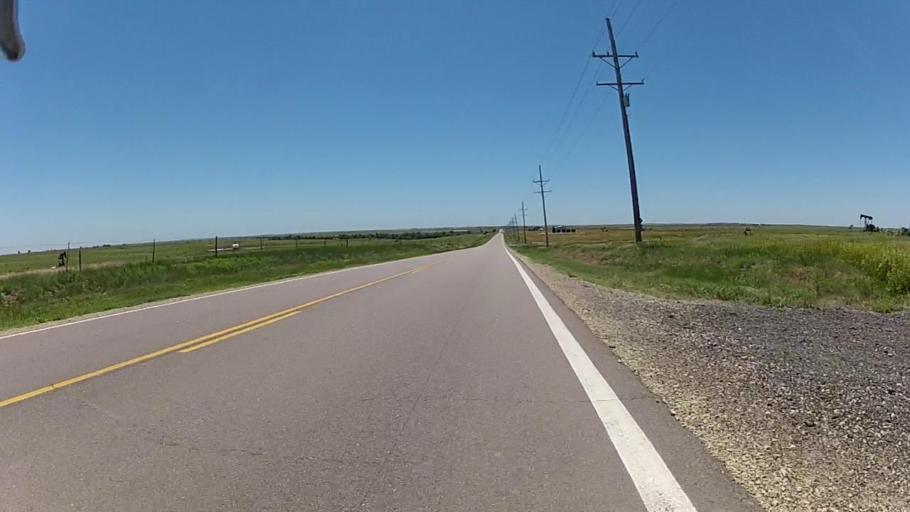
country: US
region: Kansas
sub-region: Kiowa County
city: Greensburg
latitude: 37.5128
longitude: -99.3205
